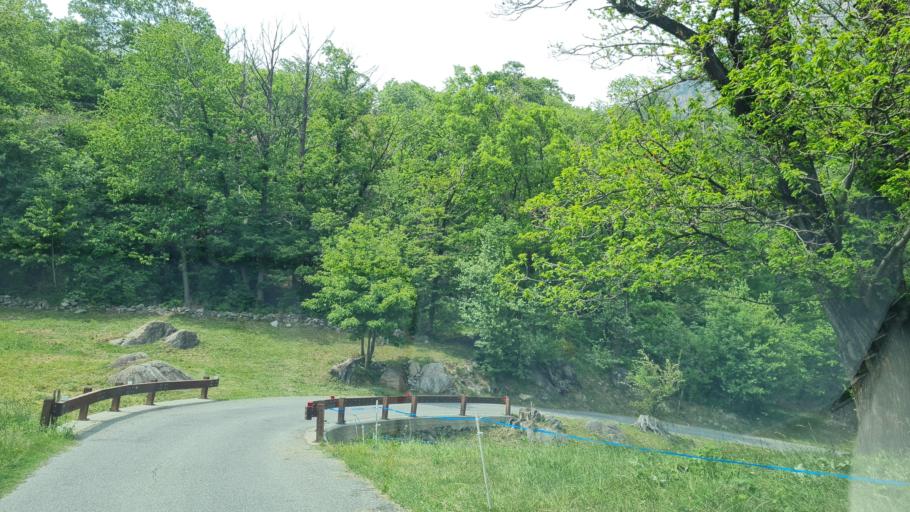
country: IT
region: Aosta Valley
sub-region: Valle d'Aosta
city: Bard
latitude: 45.6105
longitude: 7.7608
